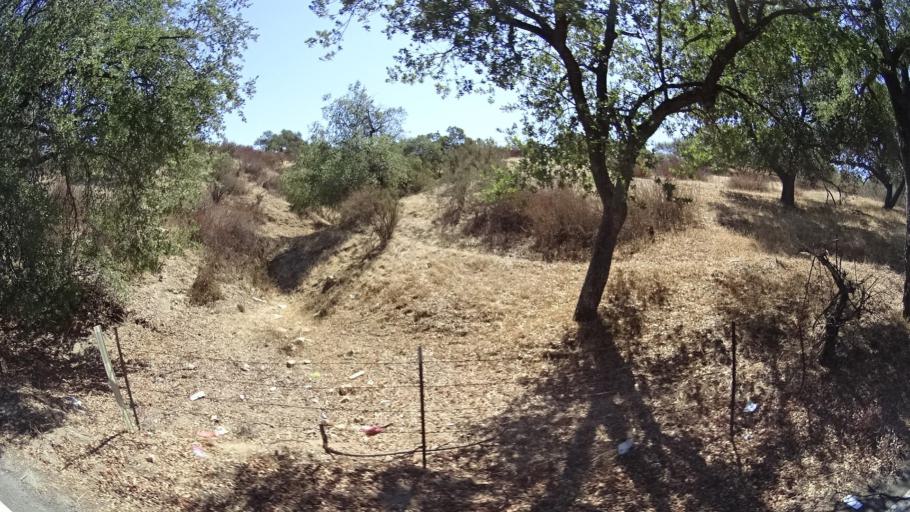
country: US
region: California
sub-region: San Diego County
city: Ramona
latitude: 33.0458
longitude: -116.8211
